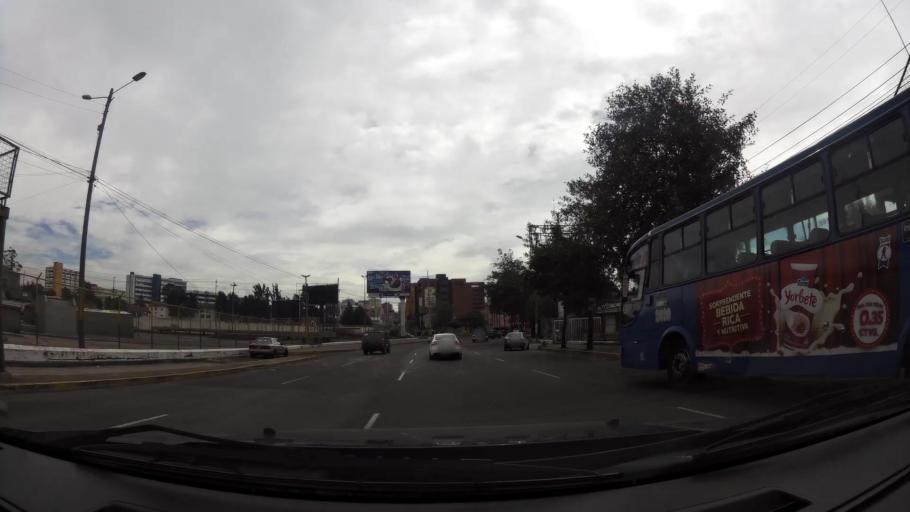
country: EC
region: Pichincha
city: Quito
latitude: -0.2137
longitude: -78.4893
